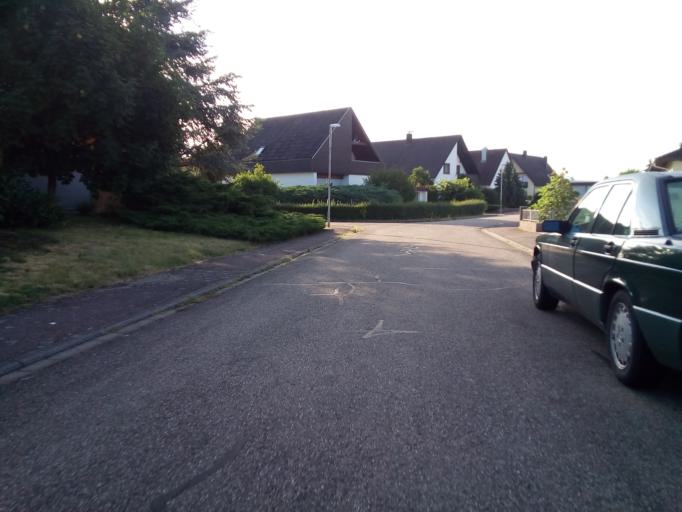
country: DE
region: Baden-Wuerttemberg
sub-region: Freiburg Region
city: Rheinau
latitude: 48.6627
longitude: 7.9416
